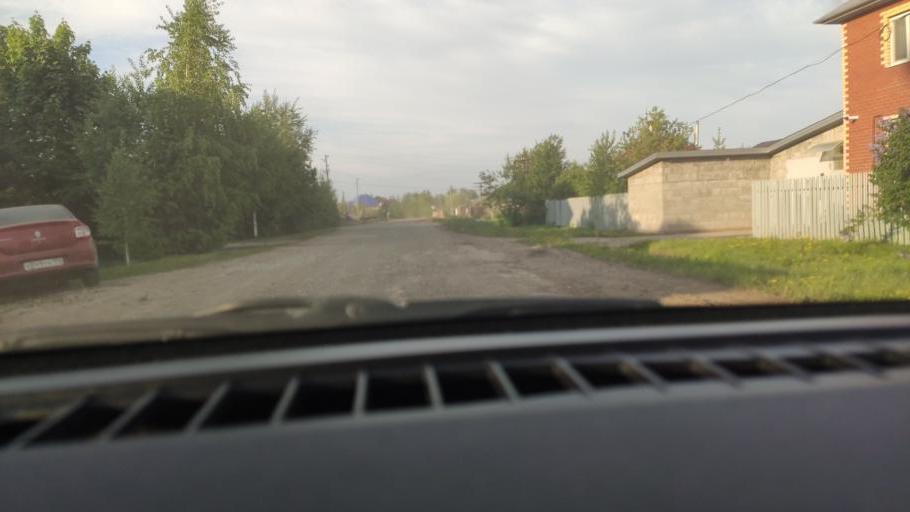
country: RU
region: Perm
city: Kultayevo
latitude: 57.9287
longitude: 56.0137
